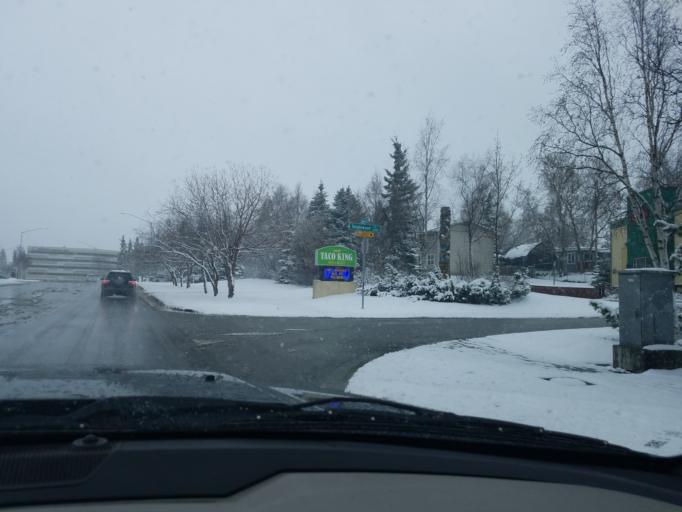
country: US
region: Alaska
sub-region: Anchorage Municipality
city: Anchorage
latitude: 61.1767
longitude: -149.9425
